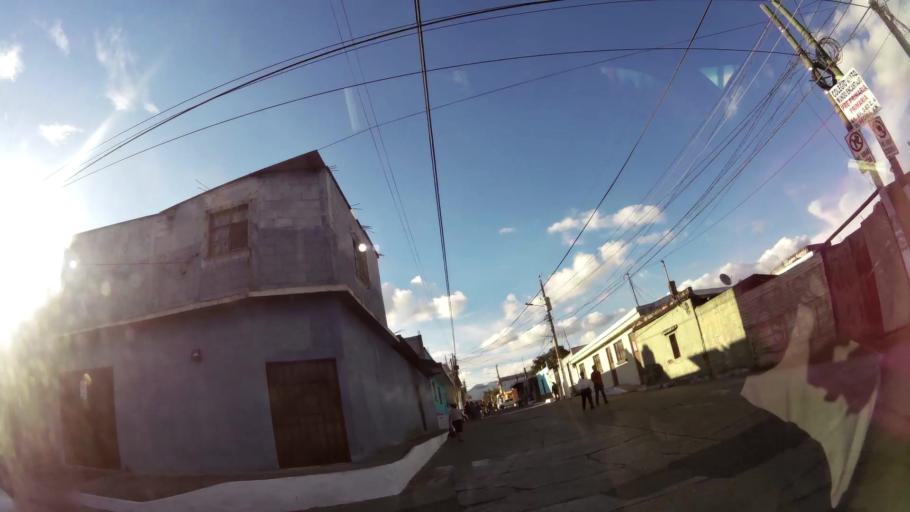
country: GT
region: Guatemala
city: Villa Nueva
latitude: 14.5234
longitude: -90.5844
